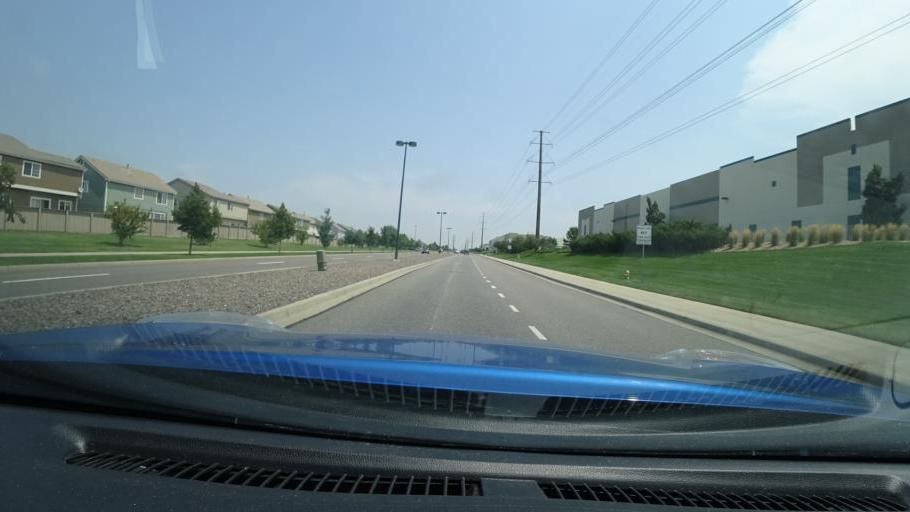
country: US
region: Colorado
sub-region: Adams County
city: Aurora
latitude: 39.7692
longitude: -104.7630
